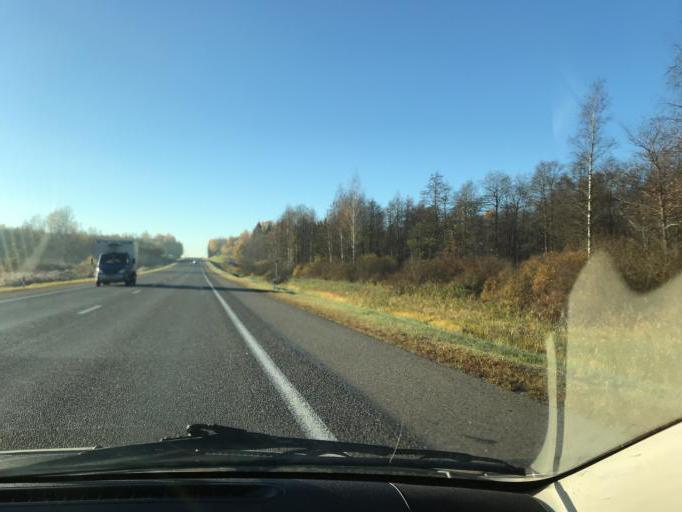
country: BY
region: Vitebsk
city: Vitebsk
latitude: 54.9193
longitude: 30.3748
